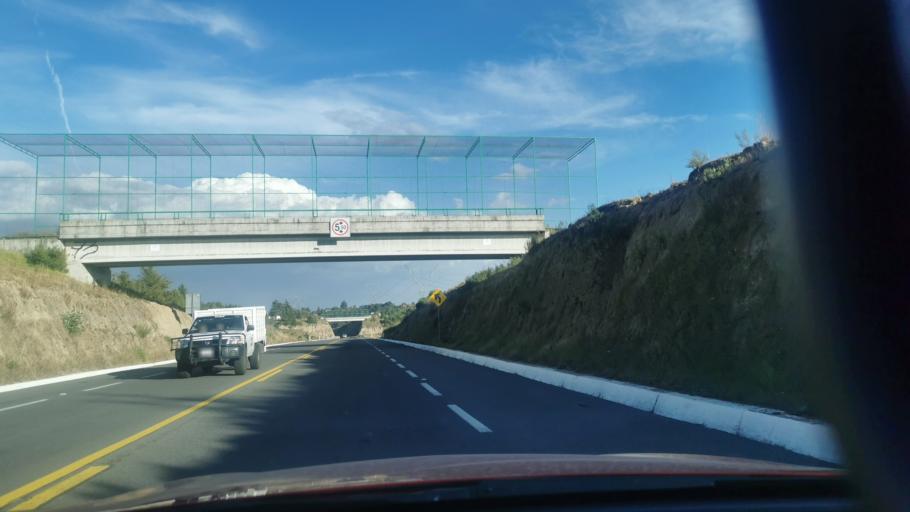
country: MX
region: Mexico
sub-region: Villa Victoria
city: Colonia Doctor Gustavo Baz
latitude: 19.3769
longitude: -99.8768
